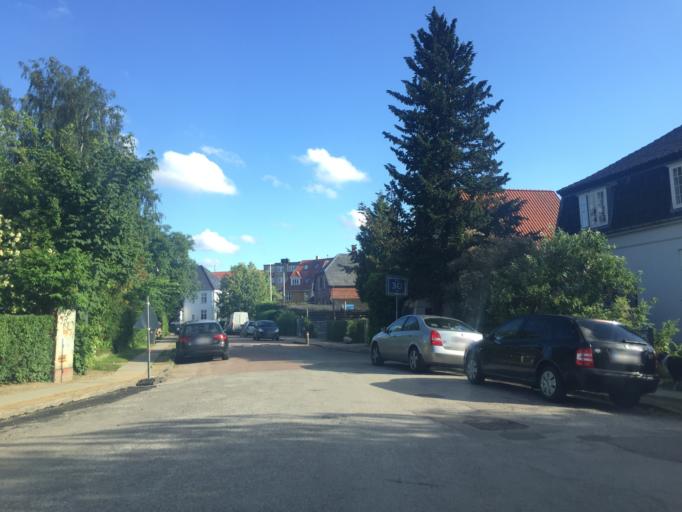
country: DK
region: Capital Region
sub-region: Kobenhavn
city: Vanlose
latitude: 55.7067
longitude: 12.4943
